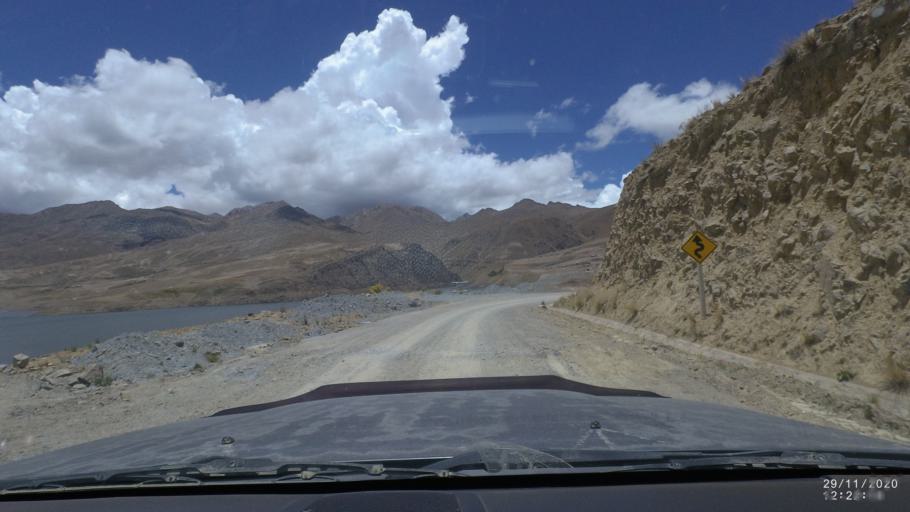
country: BO
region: Cochabamba
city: Cochabamba
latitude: -17.0975
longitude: -66.3274
